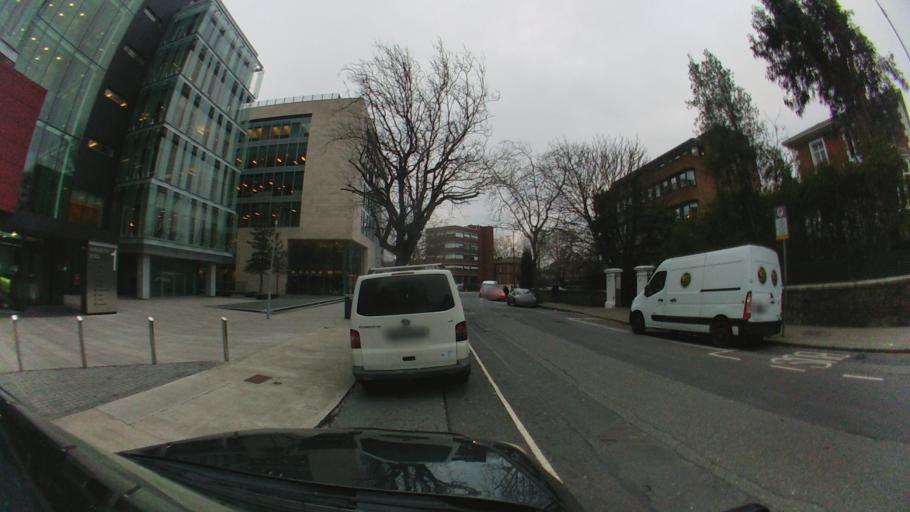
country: IE
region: Leinster
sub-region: Dublin City
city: Dublin
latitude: 53.3324
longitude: -6.2463
